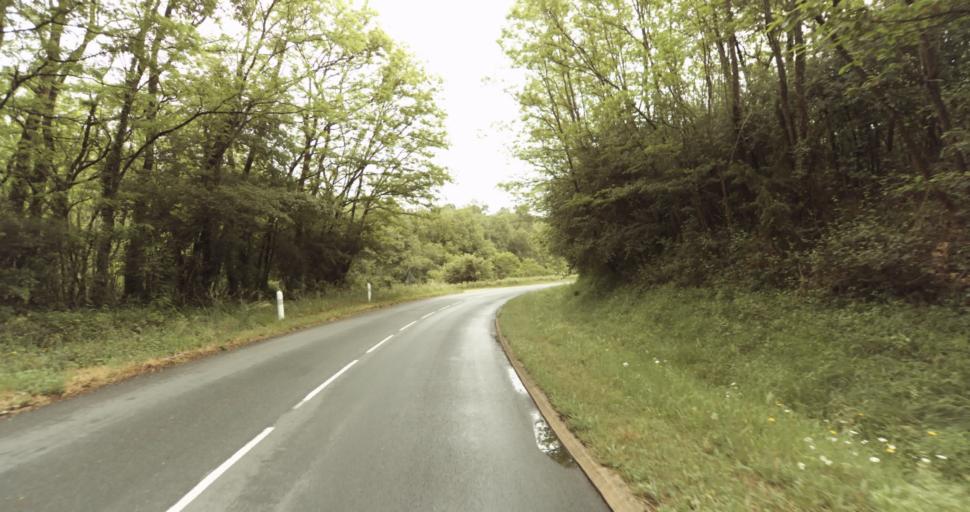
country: FR
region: Aquitaine
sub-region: Departement de la Dordogne
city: Belves
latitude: 44.7175
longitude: 0.9379
